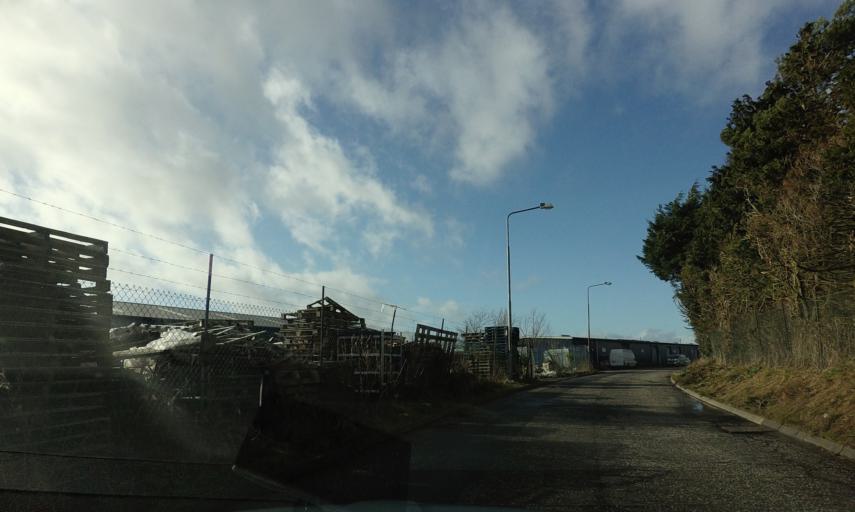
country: GB
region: Scotland
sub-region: West Lothian
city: Kirknewton
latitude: 55.8971
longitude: -3.4385
